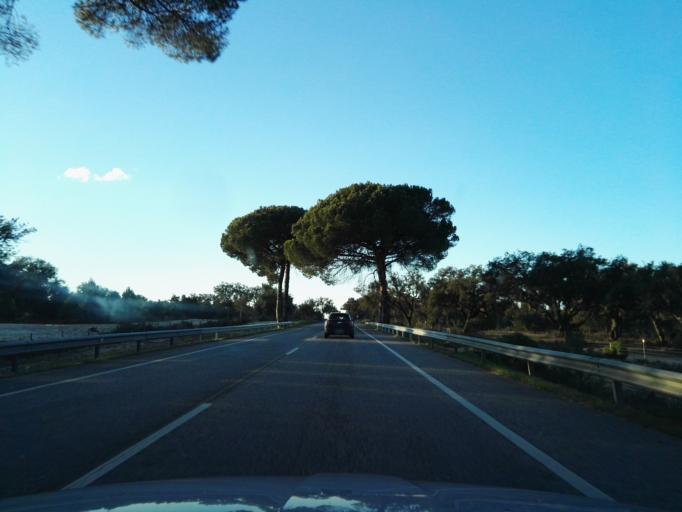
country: PT
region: Santarem
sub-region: Benavente
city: Poceirao
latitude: 38.8752
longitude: -8.8067
